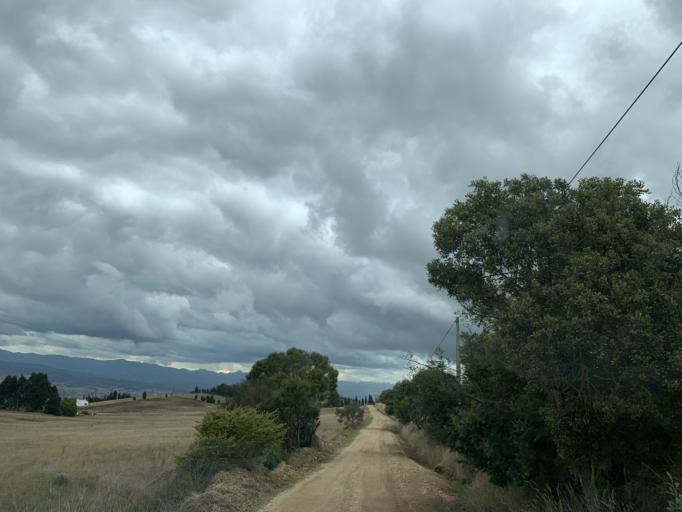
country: CO
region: Boyaca
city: Tunja
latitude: 5.5554
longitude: -73.3160
